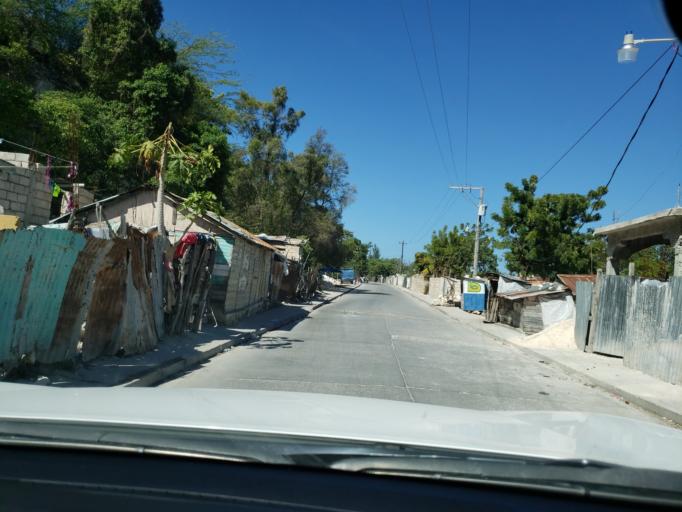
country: HT
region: Nippes
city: Miragoane
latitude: 18.4438
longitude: -73.0985
